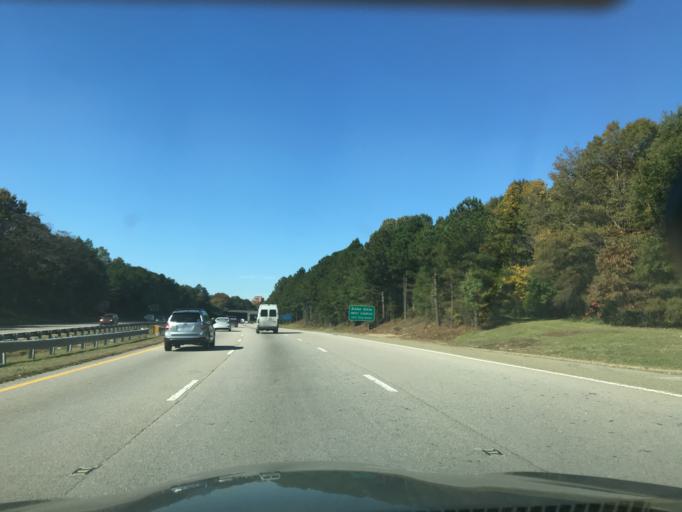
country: US
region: North Carolina
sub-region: Durham County
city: Durham
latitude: 36.0058
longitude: -78.9243
